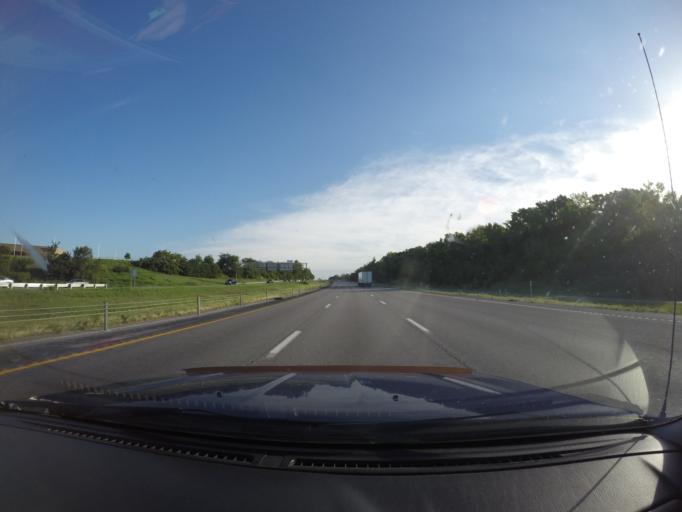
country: US
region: Missouri
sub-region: Platte County
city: Riverside
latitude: 39.1737
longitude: -94.6226
